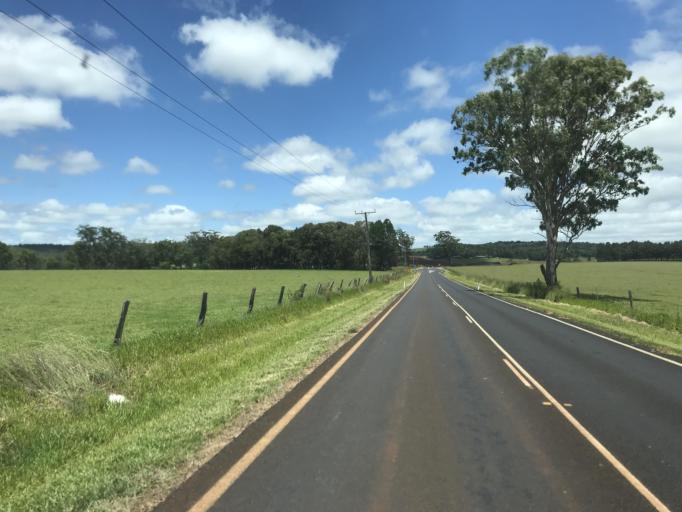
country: AU
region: Queensland
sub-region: Tablelands
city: Ravenshoe
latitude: -17.5111
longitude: 145.4532
